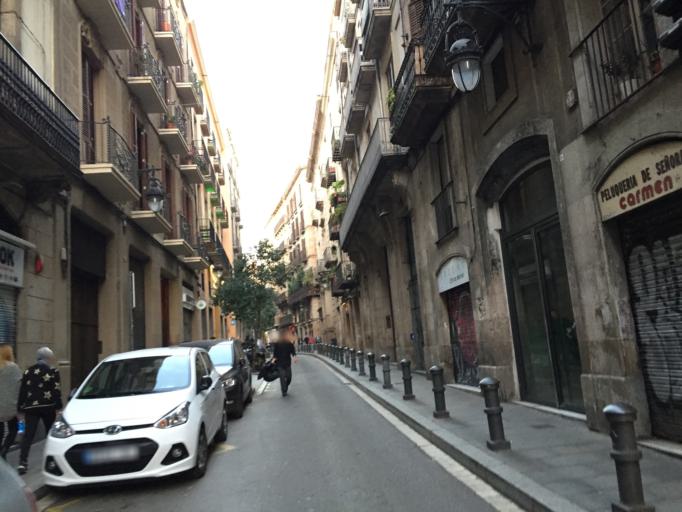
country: ES
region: Catalonia
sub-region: Provincia de Barcelona
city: Ciutat Vella
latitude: 41.3801
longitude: 2.1797
